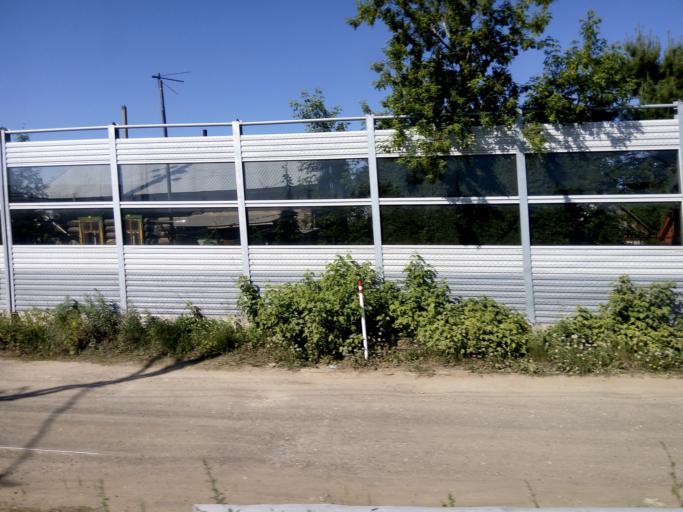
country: RU
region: Tatarstan
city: Stolbishchi
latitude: 55.6684
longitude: 49.2161
